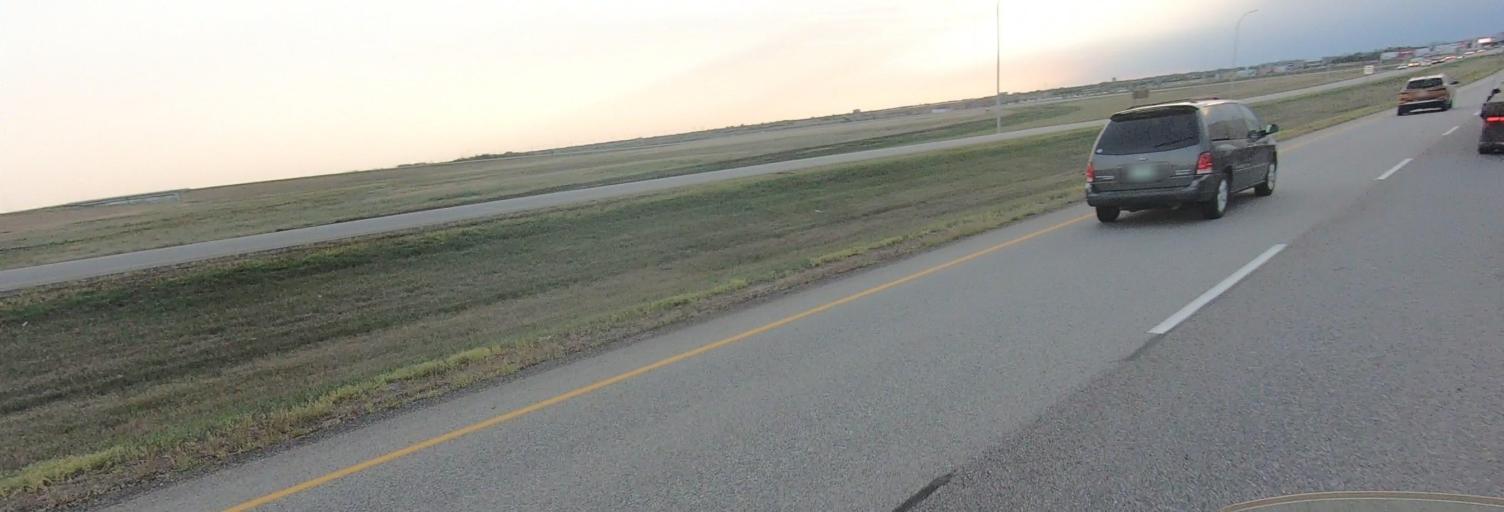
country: CA
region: Saskatchewan
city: Pilot Butte
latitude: 50.4476
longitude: -104.4965
